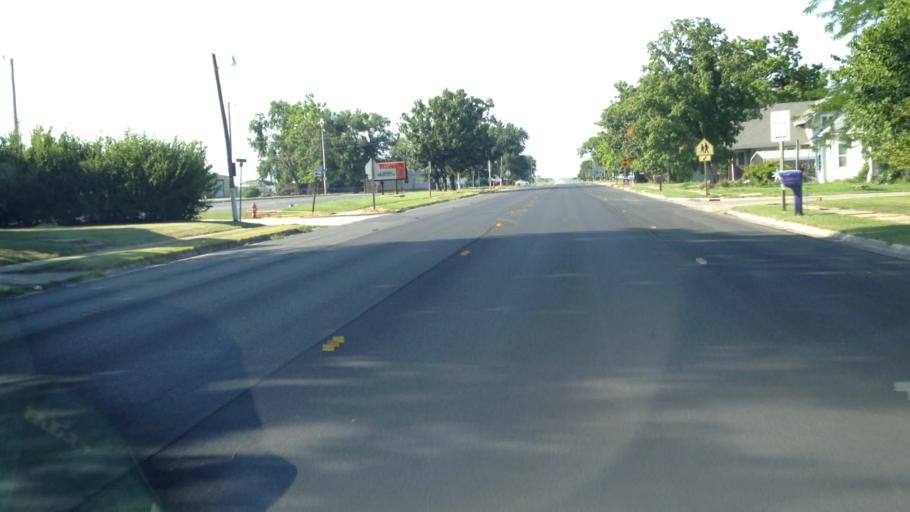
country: US
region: Kansas
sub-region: Allen County
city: Iola
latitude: 37.9183
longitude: -95.1701
